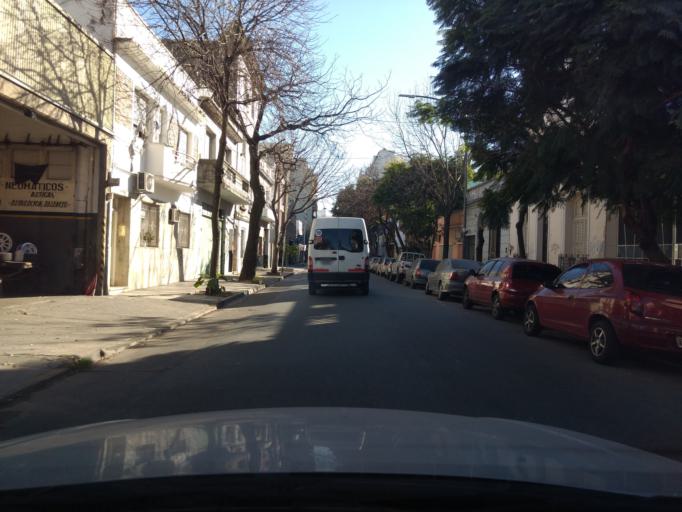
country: AR
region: Buenos Aires F.D.
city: Villa Santa Rita
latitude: -34.6193
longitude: -58.4685
